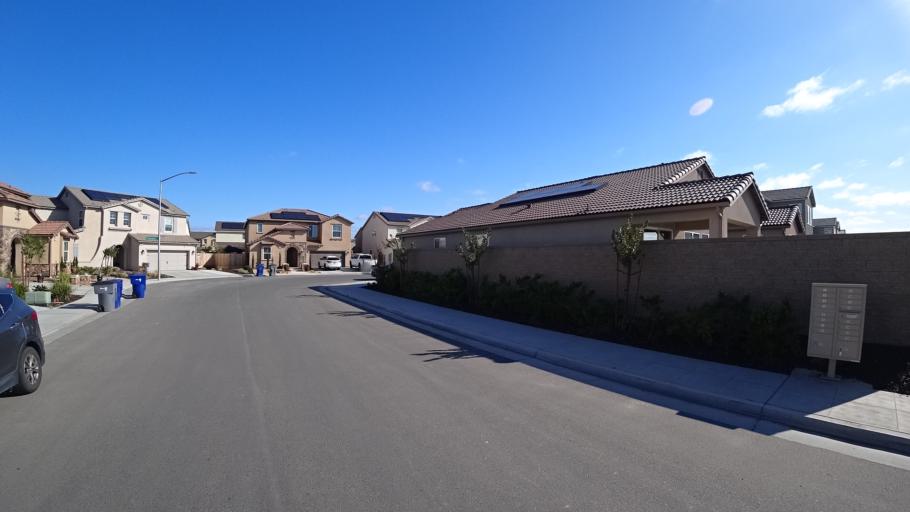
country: US
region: California
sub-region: Fresno County
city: West Park
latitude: 36.7989
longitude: -119.9044
